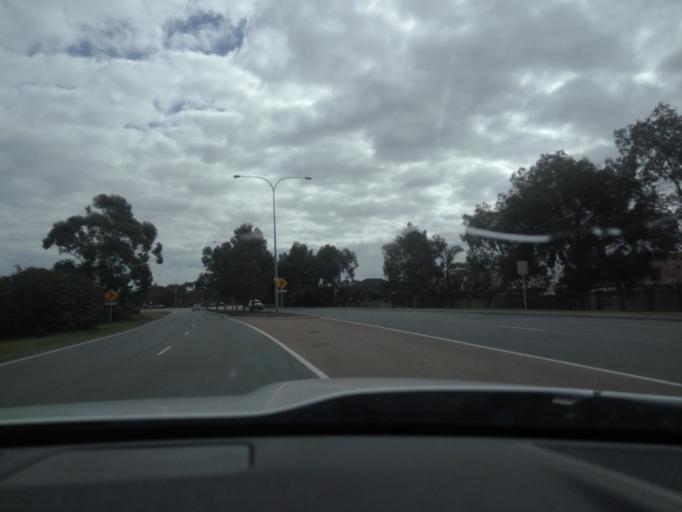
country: AU
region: Western Australia
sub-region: City of Cockburn
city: Bibra Lake
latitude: -32.1039
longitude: 115.8249
